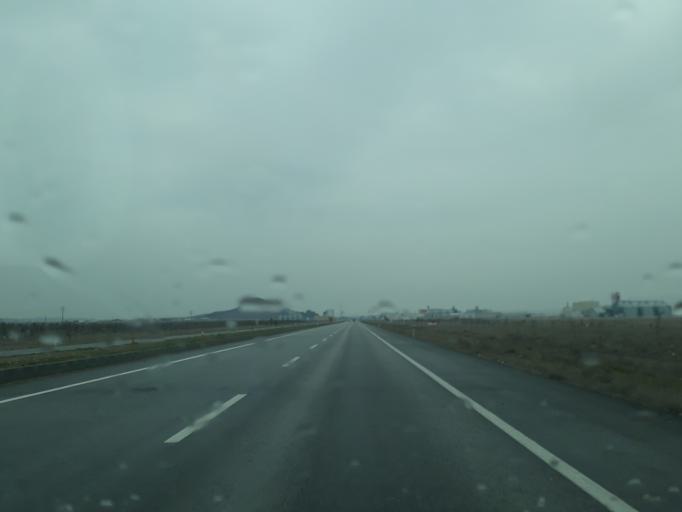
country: TR
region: Konya
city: Karapinar
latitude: 37.7124
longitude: 33.6064
